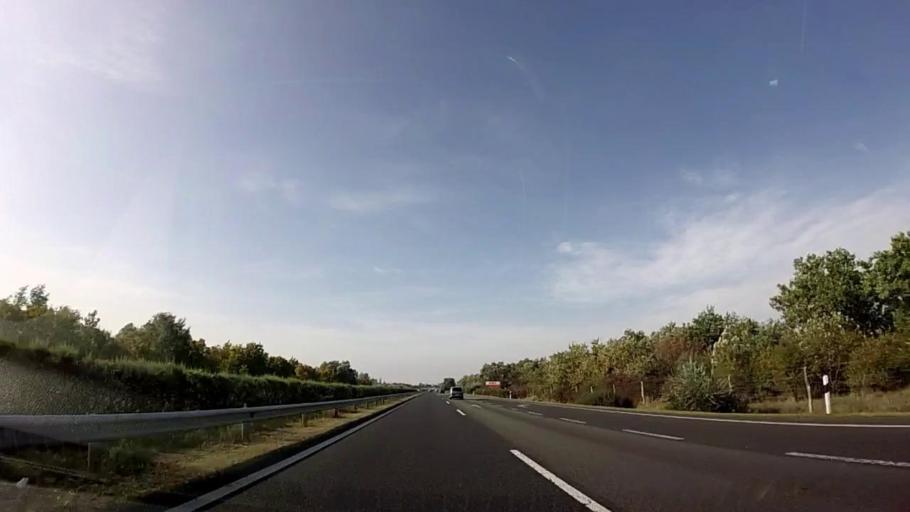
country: HU
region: Fejer
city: Pakozd
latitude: 47.1969
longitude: 18.5153
